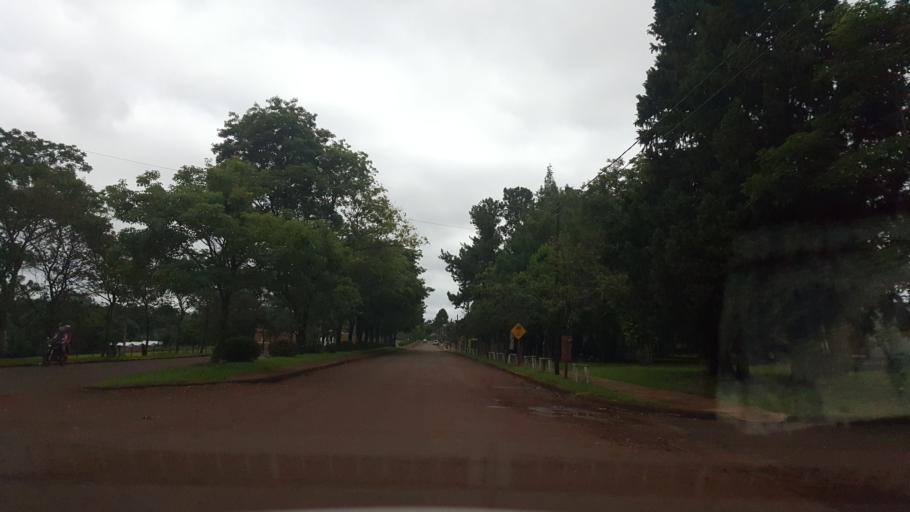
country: AR
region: Misiones
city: Ruiz de Montoya
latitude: -26.9749
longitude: -55.0517
